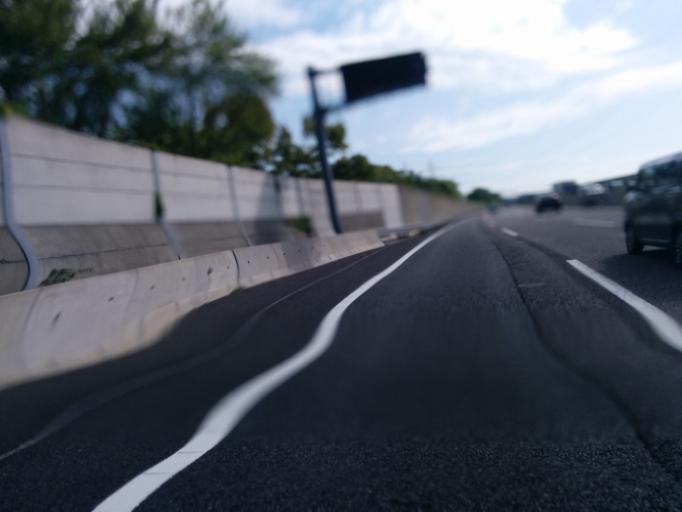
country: JP
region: Mie
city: Komono
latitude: 35.0059
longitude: 136.5710
